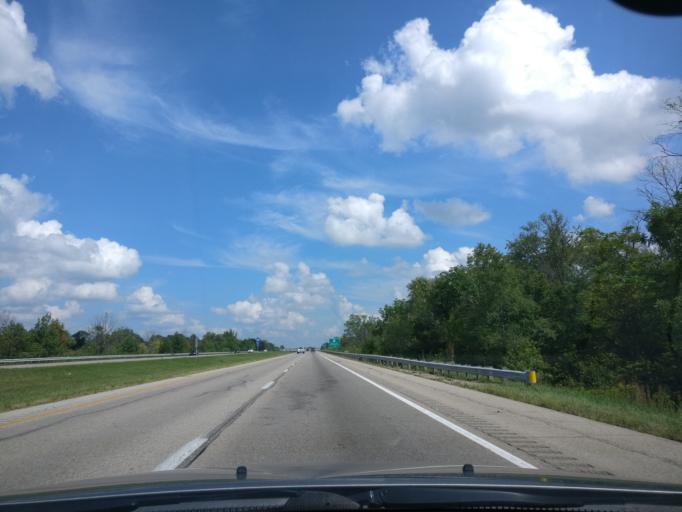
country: US
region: Ohio
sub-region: Greene County
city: Xenia
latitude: 39.6628
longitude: -83.9282
